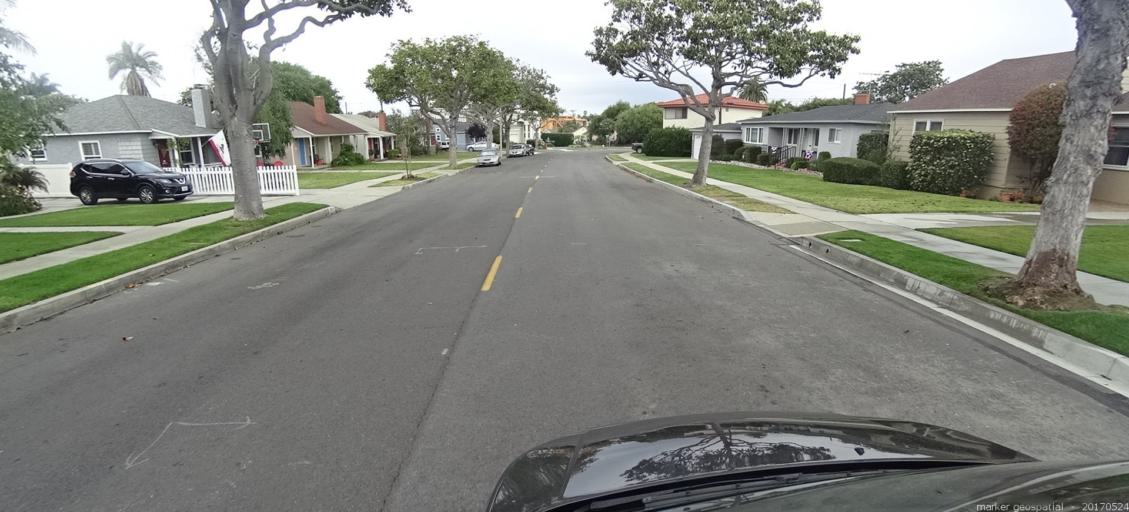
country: US
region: California
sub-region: Los Angeles County
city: Palos Verdes Estates
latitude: 33.8234
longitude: -118.3815
